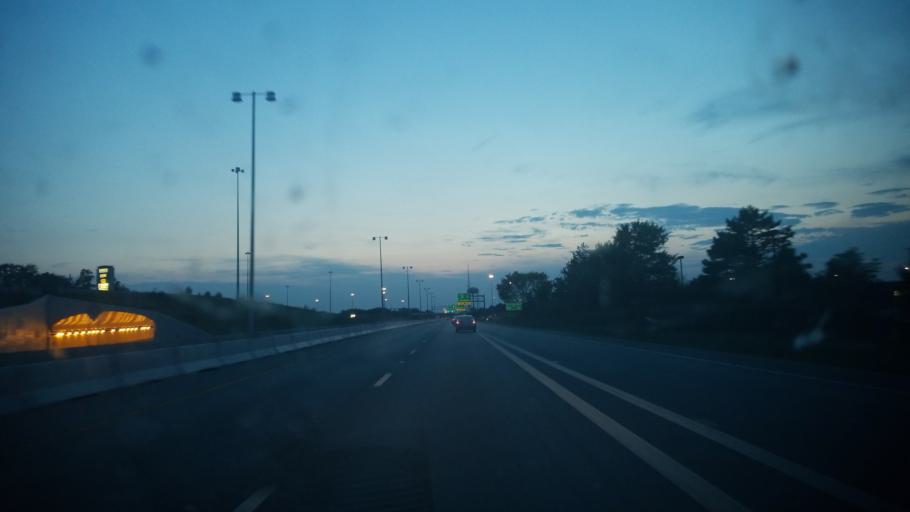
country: US
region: Ohio
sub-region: Clermont County
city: Summerside
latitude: 39.0988
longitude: -84.2752
